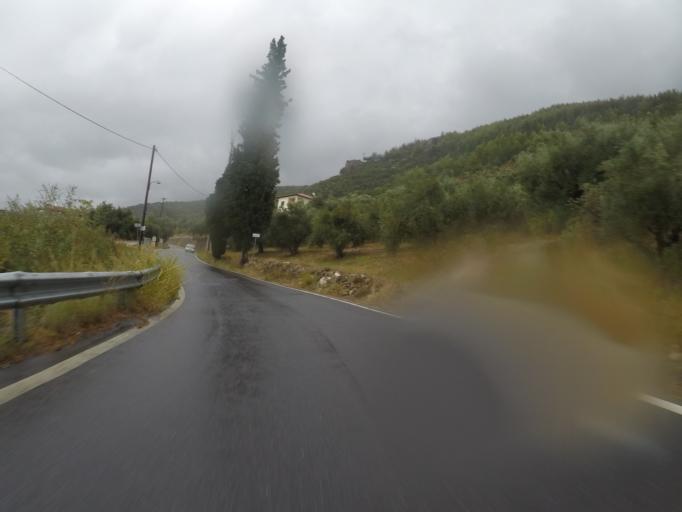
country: GR
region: Peloponnese
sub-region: Nomos Messinias
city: Kyparissia
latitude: 37.2514
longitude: 21.6809
